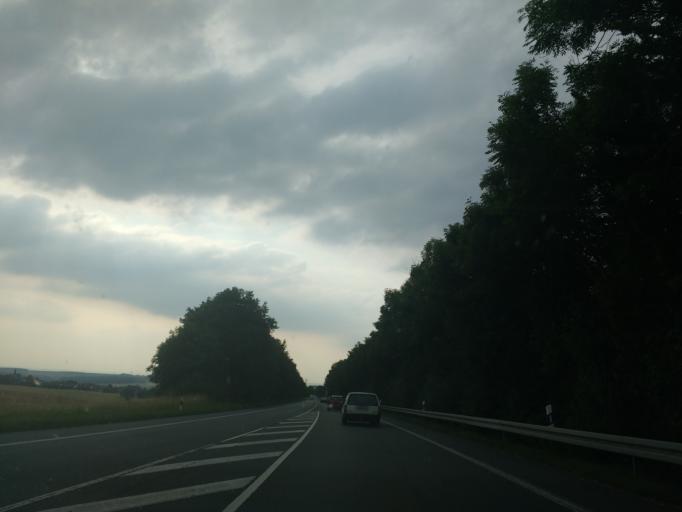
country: DE
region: North Rhine-Westphalia
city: Lichtenau
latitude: 51.6688
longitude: 8.8555
